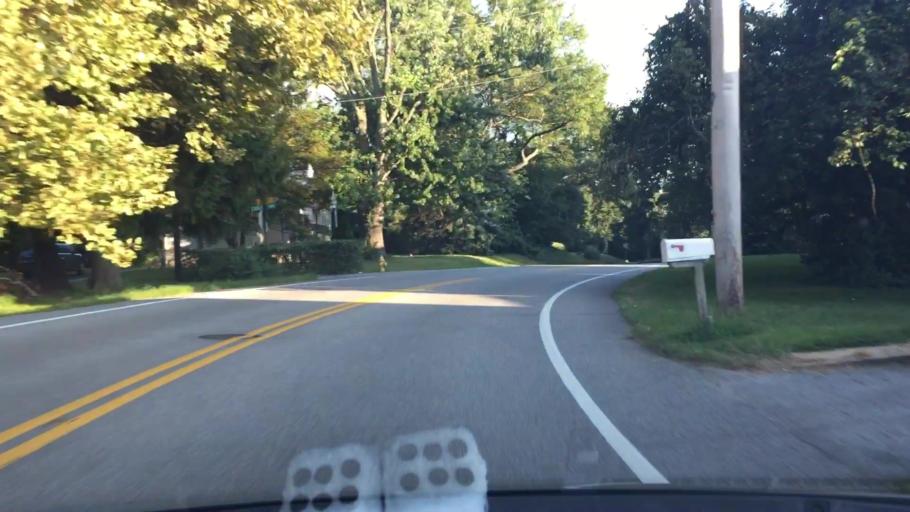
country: US
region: Pennsylvania
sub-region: Delaware County
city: Boothwyn
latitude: 39.8232
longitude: -75.4482
